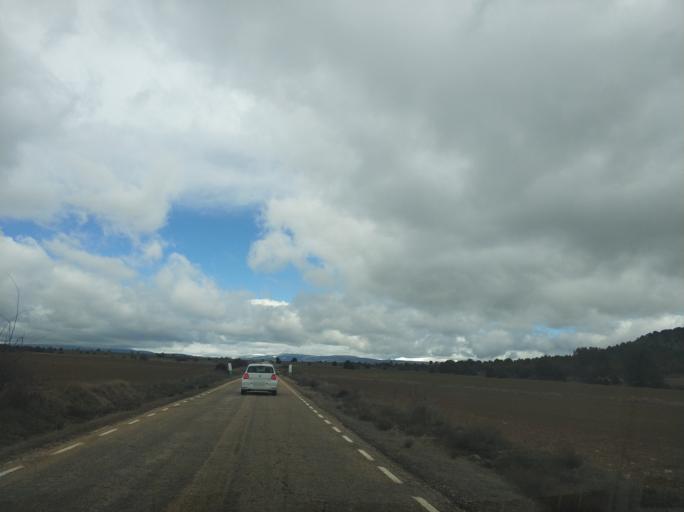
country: ES
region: Castille and Leon
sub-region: Provincia de Soria
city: Abejar
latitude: 41.7930
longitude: -2.7685
